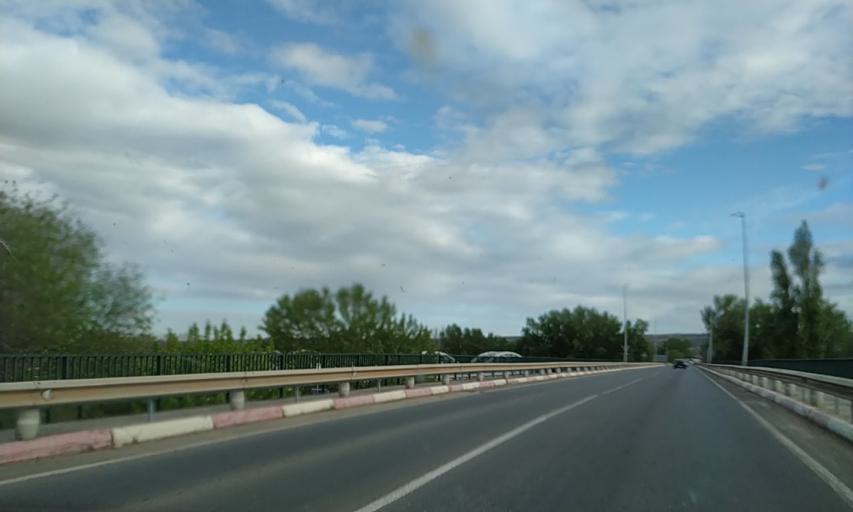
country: ES
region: Extremadura
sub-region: Provincia de Caceres
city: Coria
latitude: 39.9805
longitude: -6.5288
